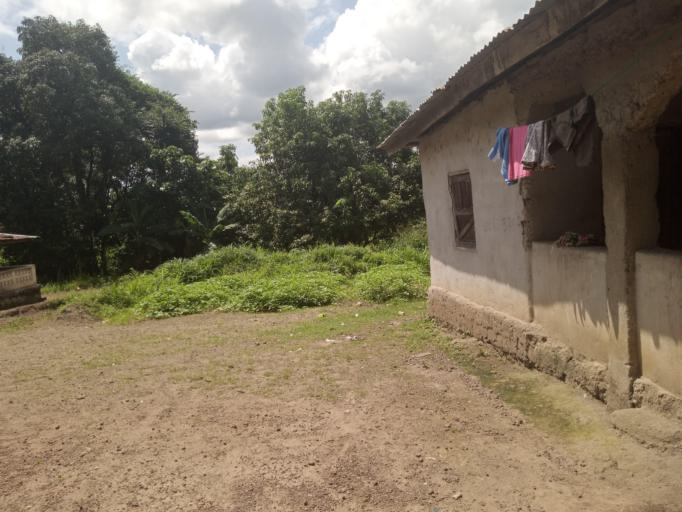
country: SL
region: Northern Province
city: Kamakwie
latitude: 9.4991
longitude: -12.2432
